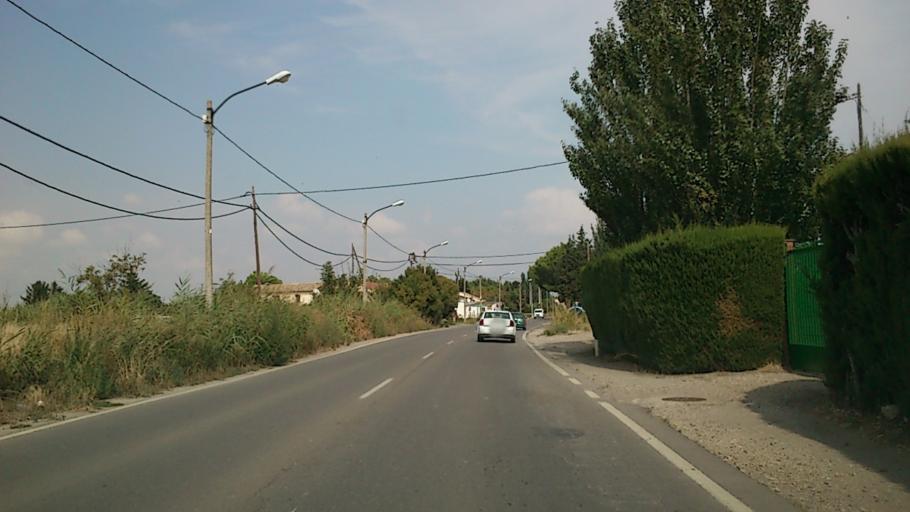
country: ES
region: Aragon
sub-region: Provincia de Zaragoza
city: Villanueva de Gallego
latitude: 41.7066
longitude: -0.8141
